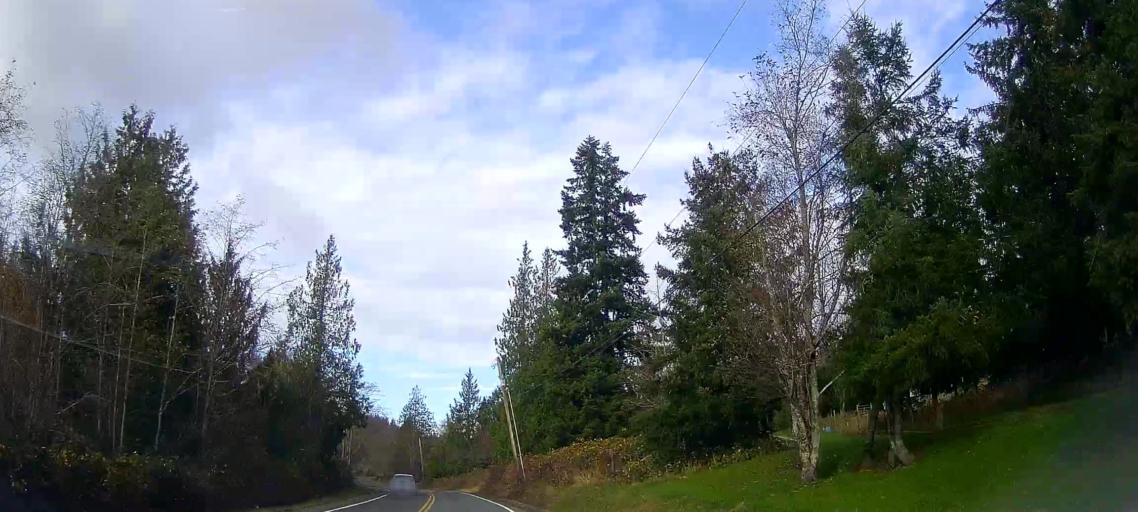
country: US
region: Washington
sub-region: Skagit County
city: Big Lake
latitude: 48.4138
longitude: -122.2227
